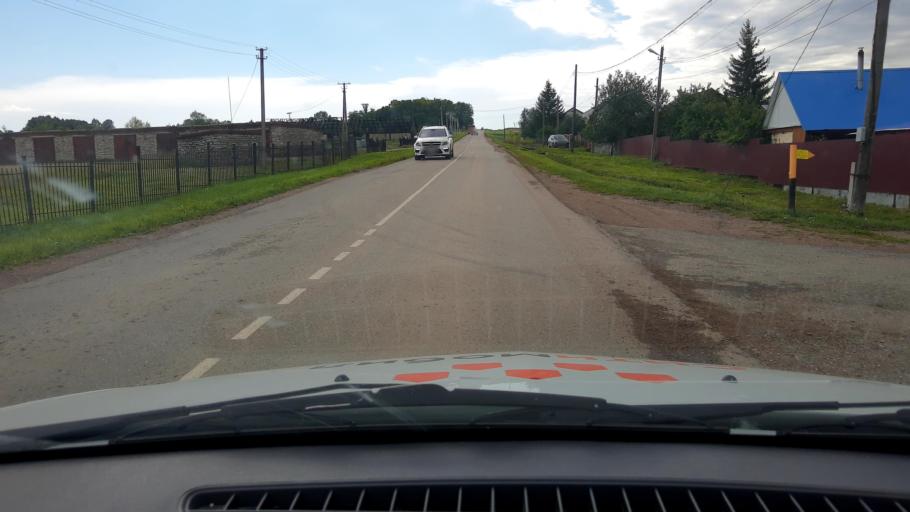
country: RU
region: Bashkortostan
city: Iglino
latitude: 54.9048
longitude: 56.1967
